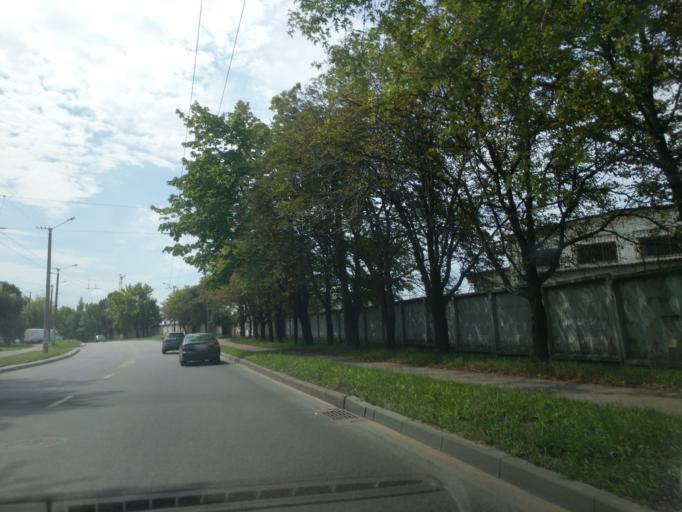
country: BY
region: Minsk
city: Novoye Medvezhino
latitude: 53.8905
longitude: 27.4822
